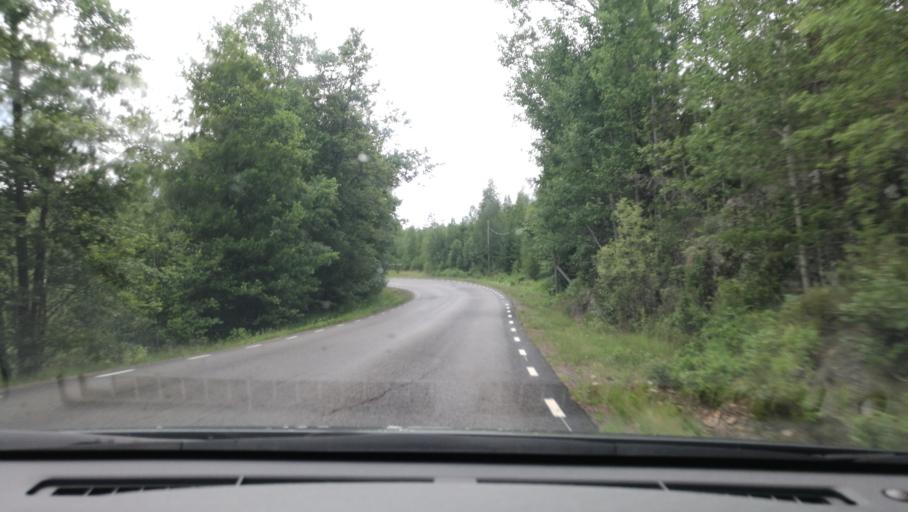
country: SE
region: OEstergoetland
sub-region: Norrkopings Kommun
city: Jursla
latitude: 58.8055
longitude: 16.1230
